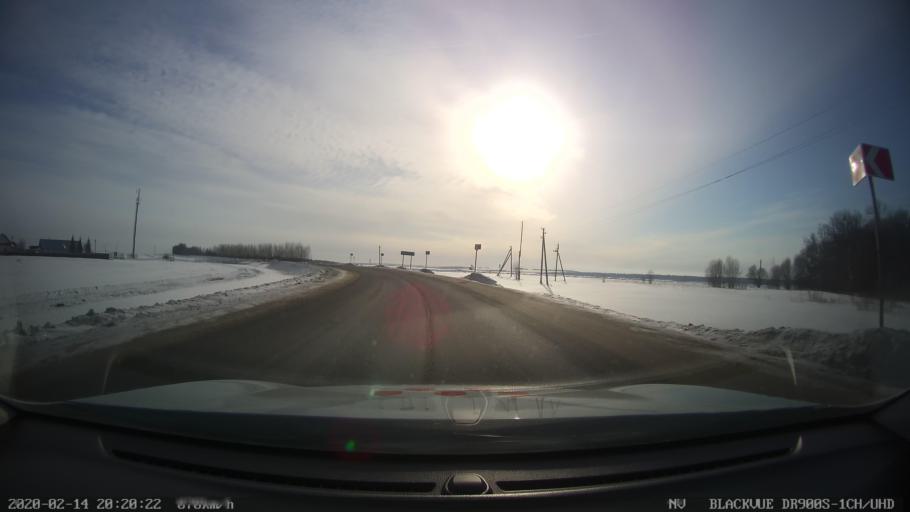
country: RU
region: Tatarstan
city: Verkhniy Uslon
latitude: 55.5578
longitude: 48.9051
